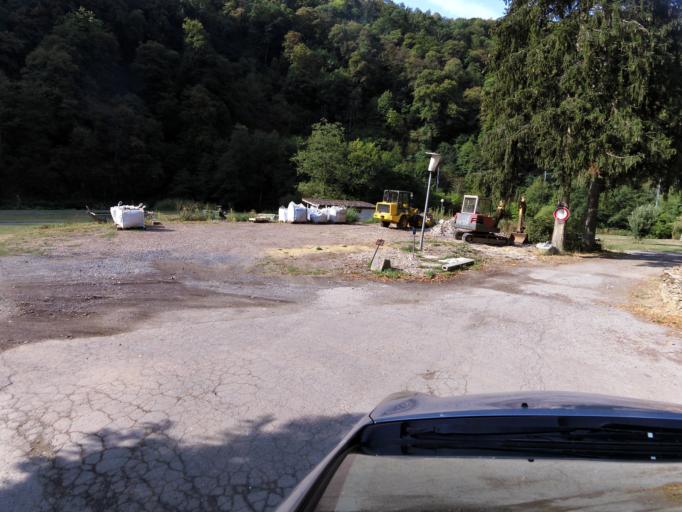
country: LU
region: Diekirch
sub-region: Canton de Diekirch
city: Bourscheid
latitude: 49.9084
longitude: 6.0798
